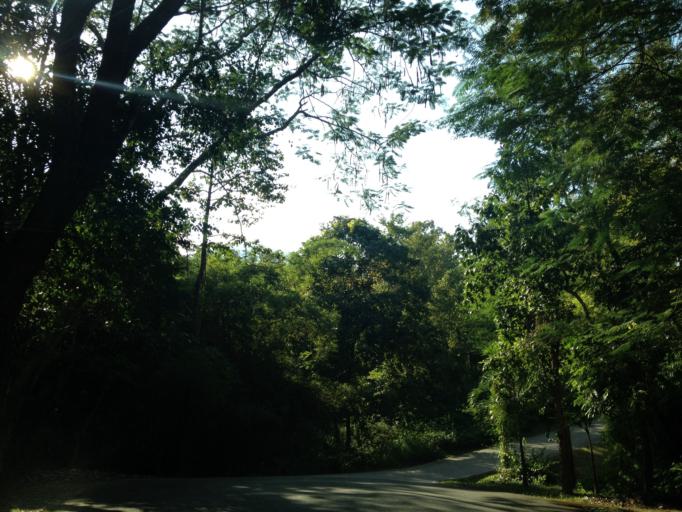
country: TH
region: Chiang Mai
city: Chiang Mai
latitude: 18.8656
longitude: 98.9382
